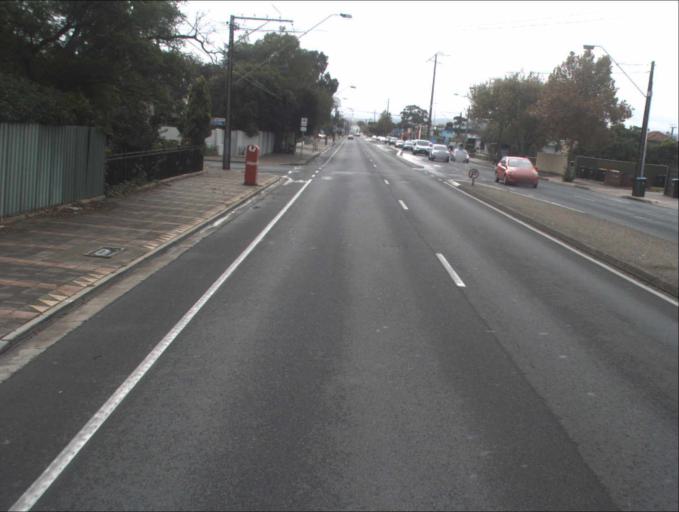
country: AU
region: South Australia
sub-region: Port Adelaide Enfield
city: Klemzig
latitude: -34.8792
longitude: 138.6265
